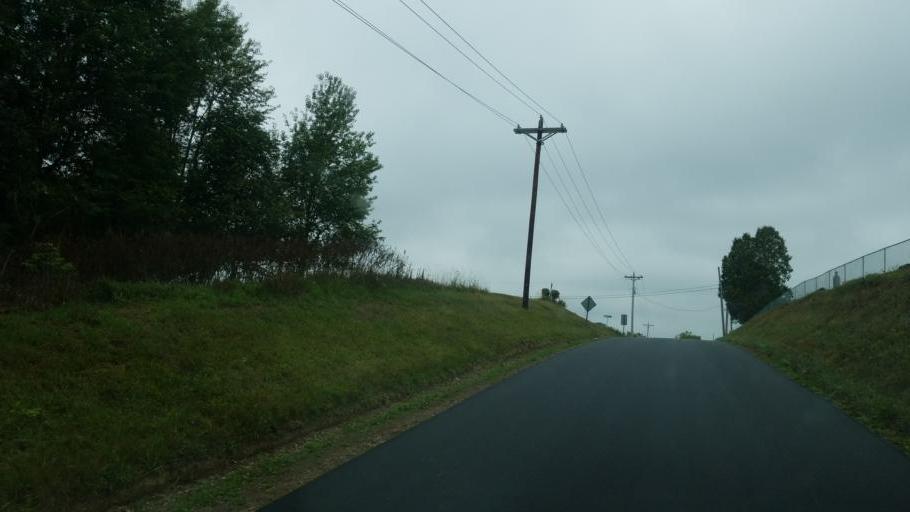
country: US
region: Ohio
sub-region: Licking County
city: Utica
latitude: 40.2417
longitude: -82.3818
